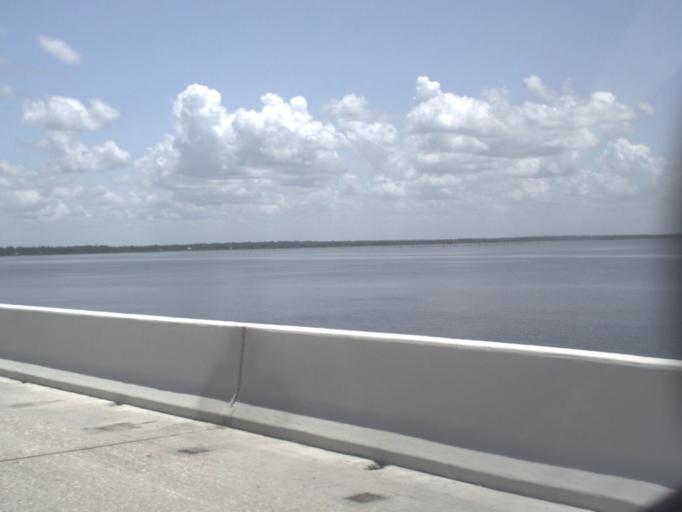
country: US
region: Florida
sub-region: Walton County
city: Freeport
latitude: 30.4112
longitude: -86.1631
